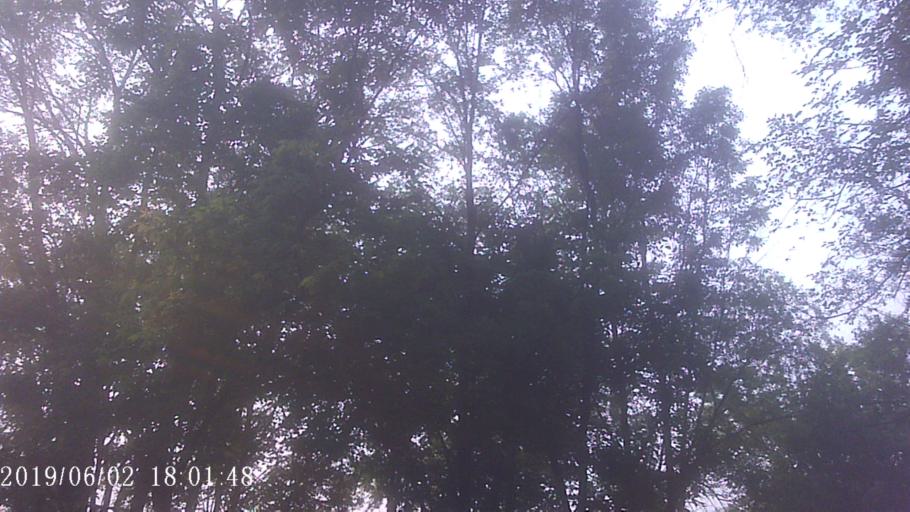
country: US
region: Minnesota
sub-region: Dakota County
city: West Saint Paul
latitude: 44.9305
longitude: -93.1049
